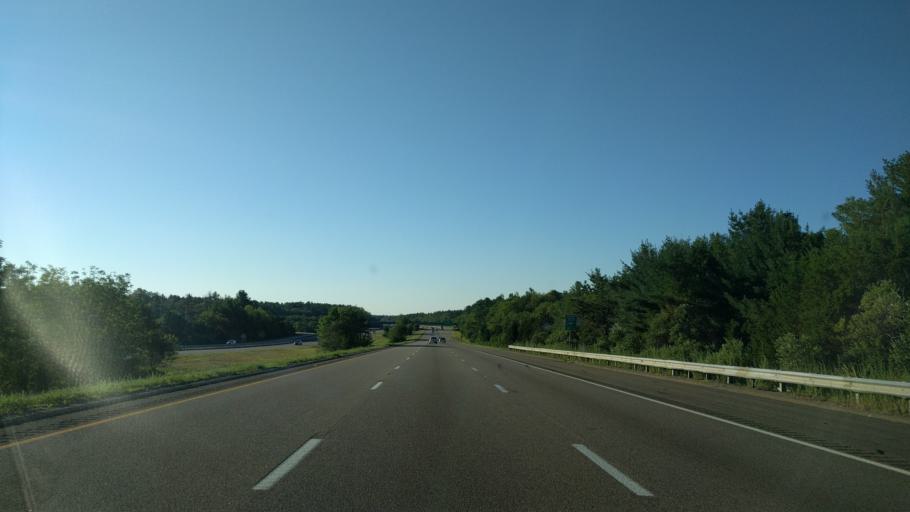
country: US
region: Massachusetts
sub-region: Bristol County
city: Mansfield Center
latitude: 42.0110
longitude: -71.2312
